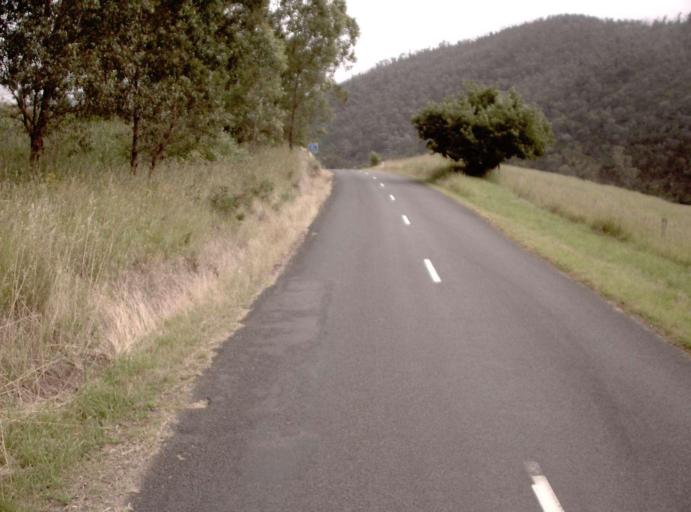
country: AU
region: Victoria
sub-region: Wellington
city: Heyfield
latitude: -37.7669
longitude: 146.6679
